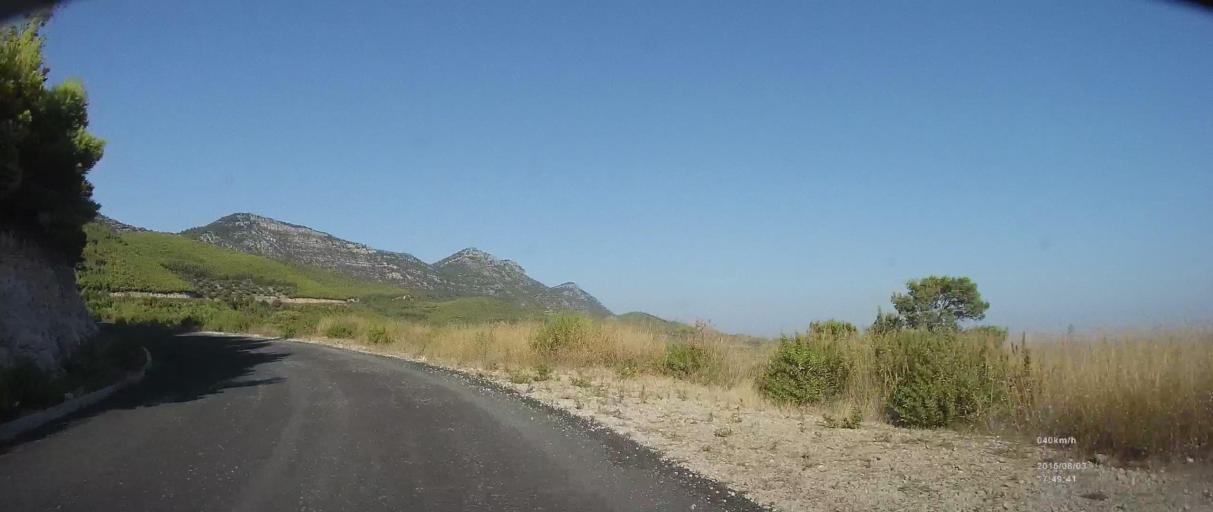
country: HR
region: Dubrovacko-Neretvanska
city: Blato
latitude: 42.7355
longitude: 17.5169
